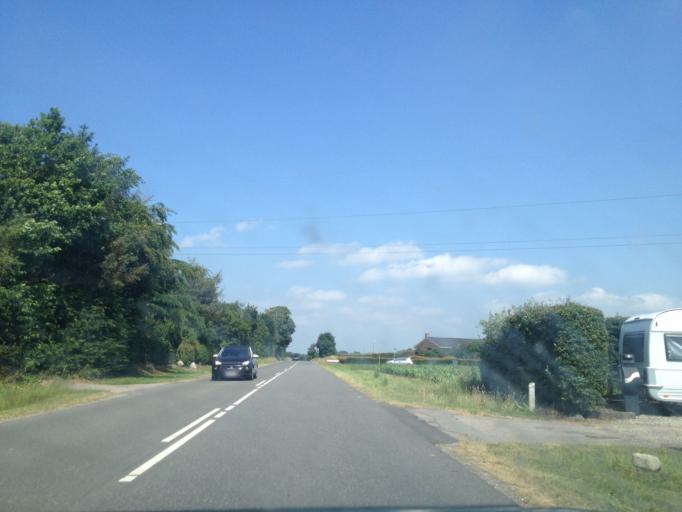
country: DK
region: South Denmark
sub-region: Kolding Kommune
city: Vamdrup
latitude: 55.4105
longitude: 9.2553
